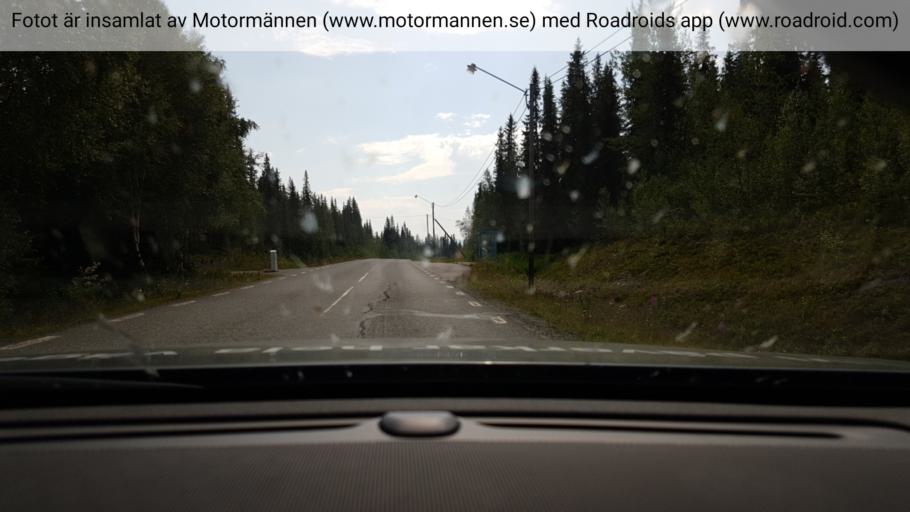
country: SE
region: Vaesterbotten
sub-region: Vilhelmina Kommun
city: Sjoberg
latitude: 65.4497
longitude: 16.1011
